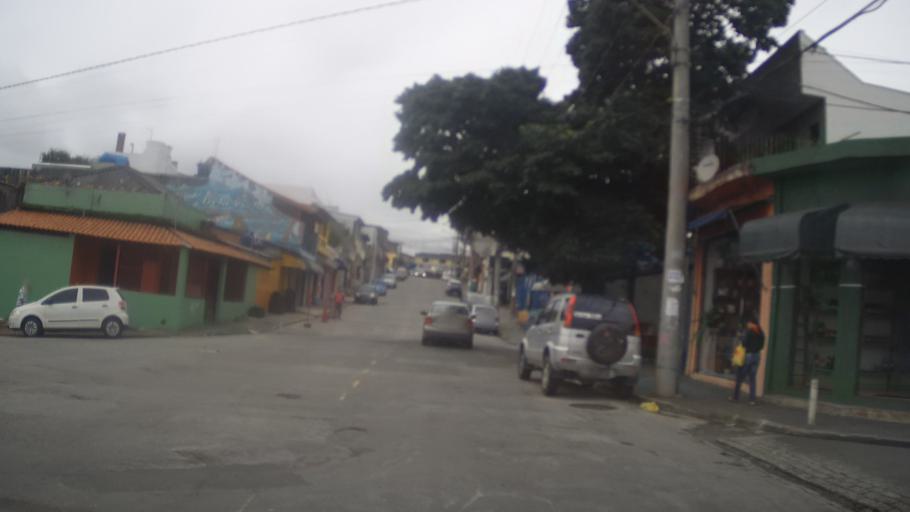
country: BR
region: Sao Paulo
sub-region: Guarulhos
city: Guarulhos
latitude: -23.4395
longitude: -46.5120
